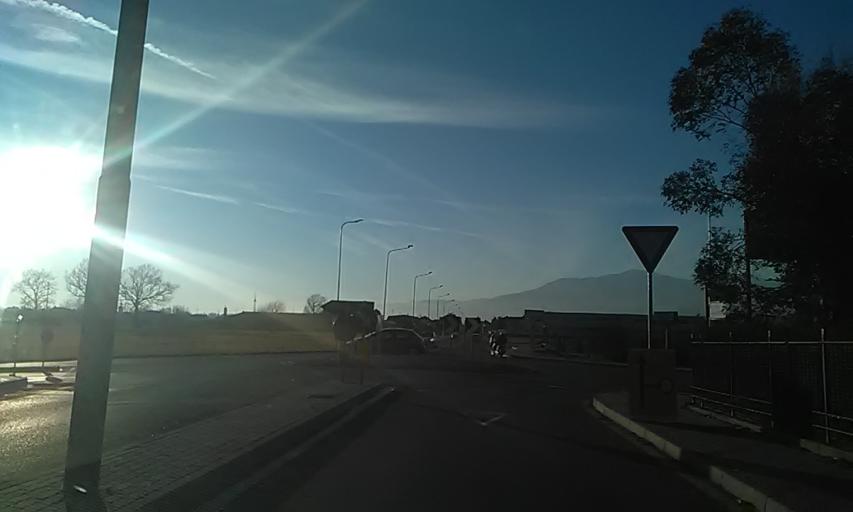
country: IT
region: Piedmont
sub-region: Provincia di Biella
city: Valdengo
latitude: 45.5635
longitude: 8.1391
